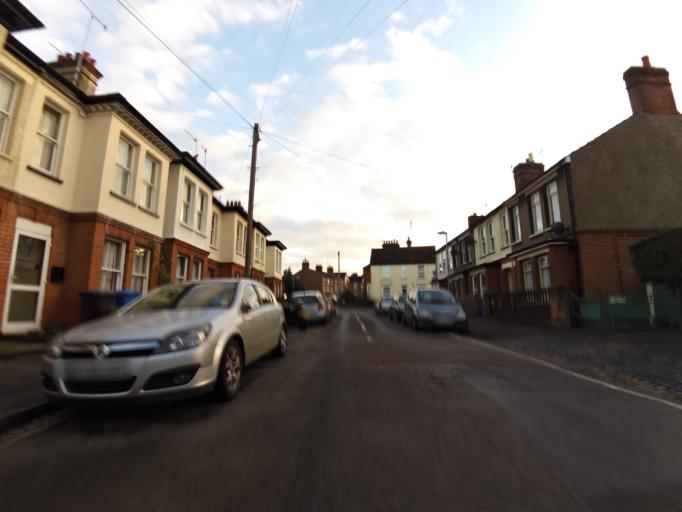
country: GB
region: England
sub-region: Suffolk
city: Ipswich
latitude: 52.0502
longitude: 1.1516
